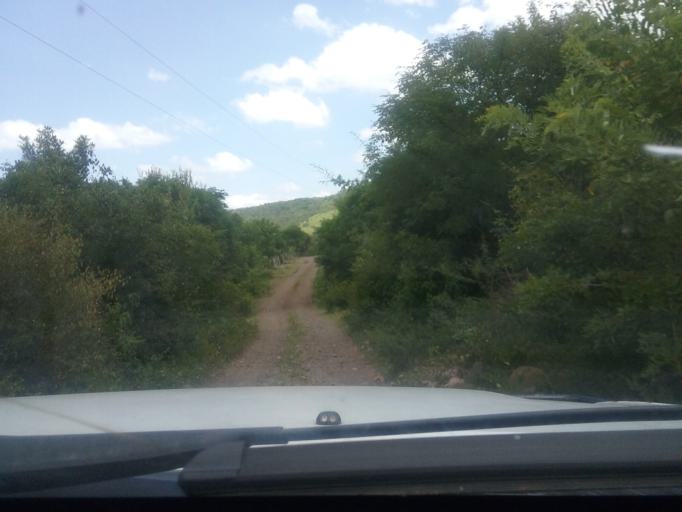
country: NI
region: Matagalpa
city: Terrabona
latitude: 12.6517
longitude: -85.9995
